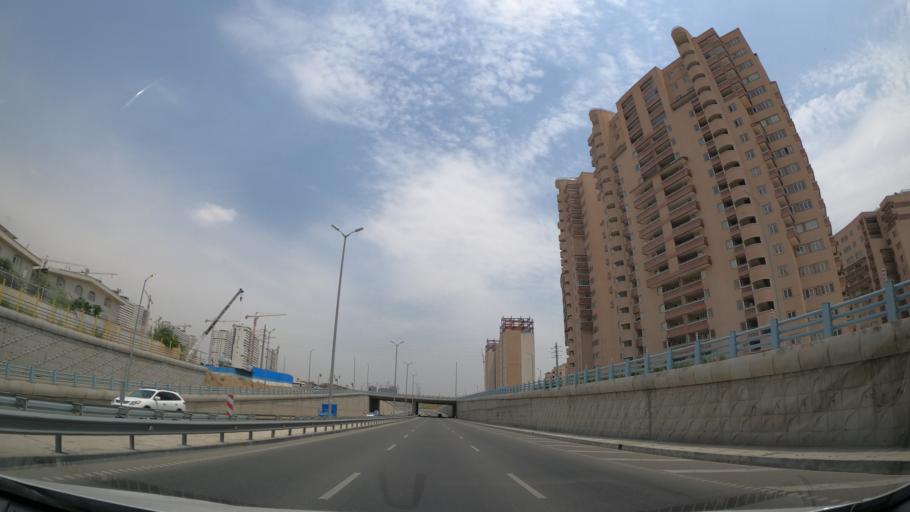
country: IR
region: Tehran
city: Shahr-e Qods
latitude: 35.7514
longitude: 51.1546
